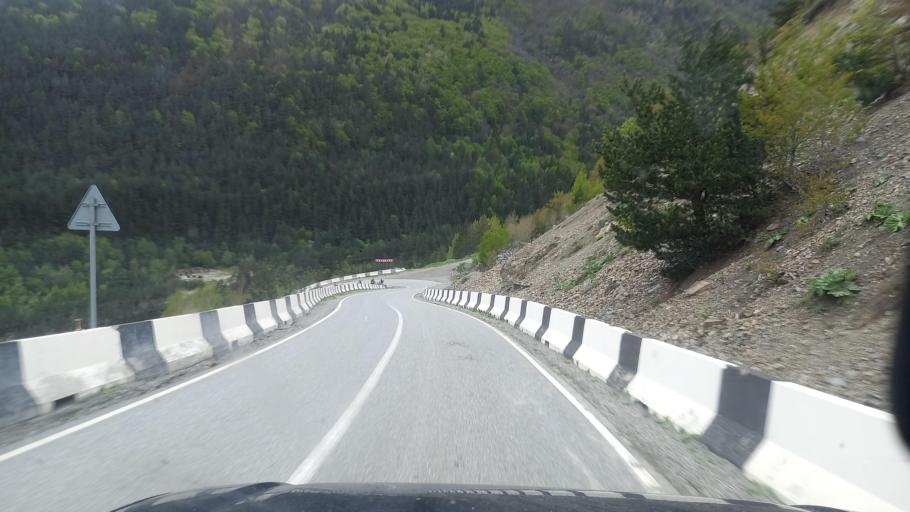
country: RU
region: North Ossetia
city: Mizur
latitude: 42.7928
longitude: 43.9998
